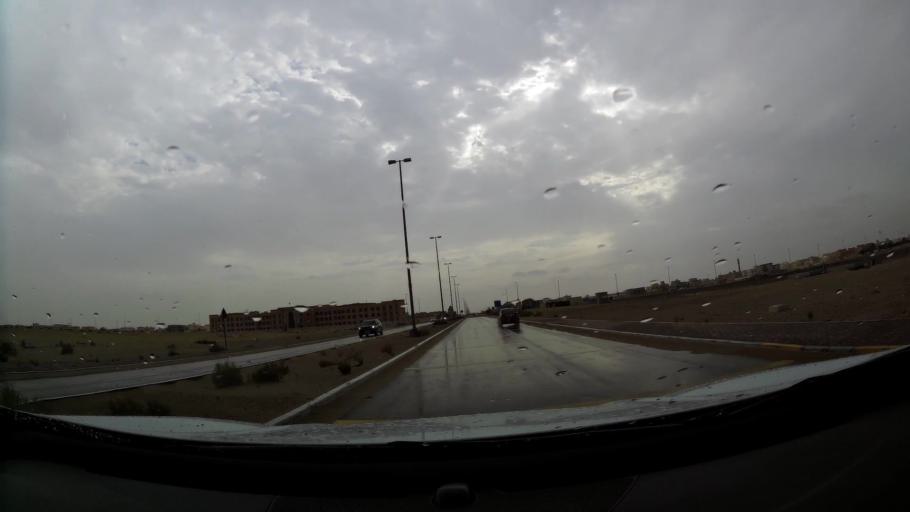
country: AE
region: Abu Dhabi
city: Abu Dhabi
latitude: 24.3643
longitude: 54.6345
